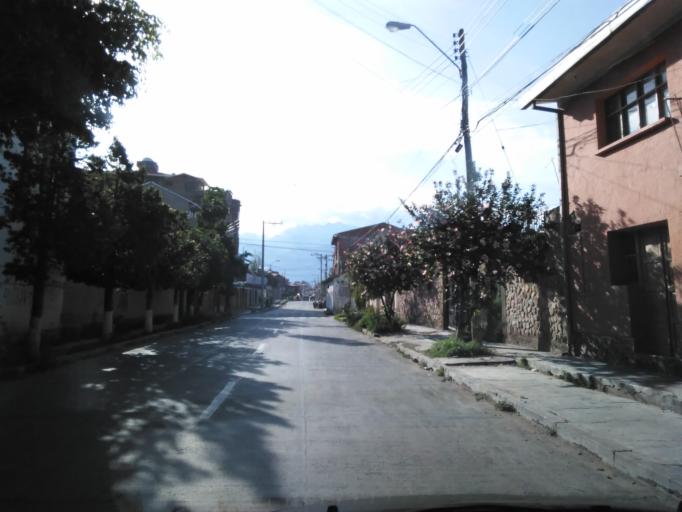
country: BO
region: Cochabamba
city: Cochabamba
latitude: -17.3384
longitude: -66.2169
